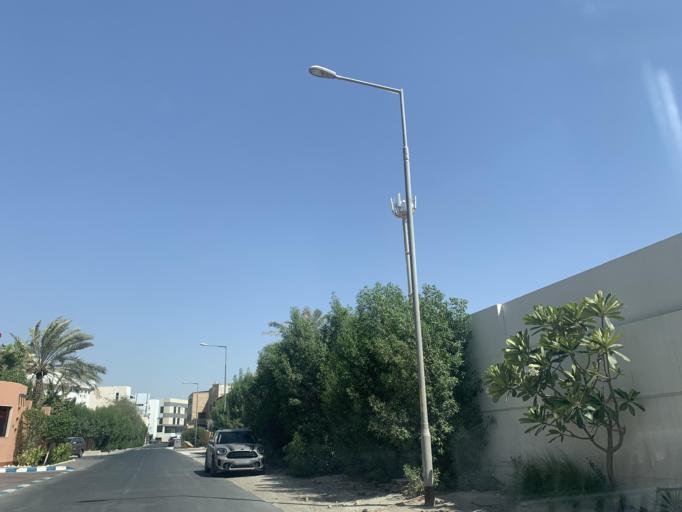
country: BH
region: Manama
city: Jidd Hafs
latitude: 26.2225
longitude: 50.5010
